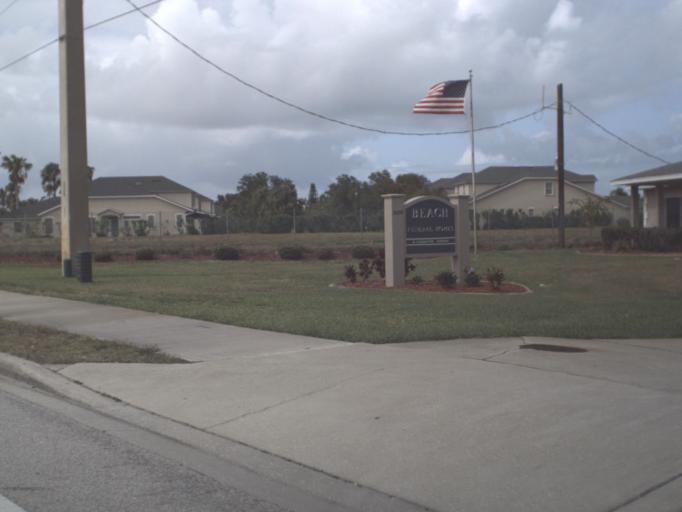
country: US
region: Florida
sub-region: Brevard County
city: Indian Harbour Beach
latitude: 28.1607
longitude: -80.6042
